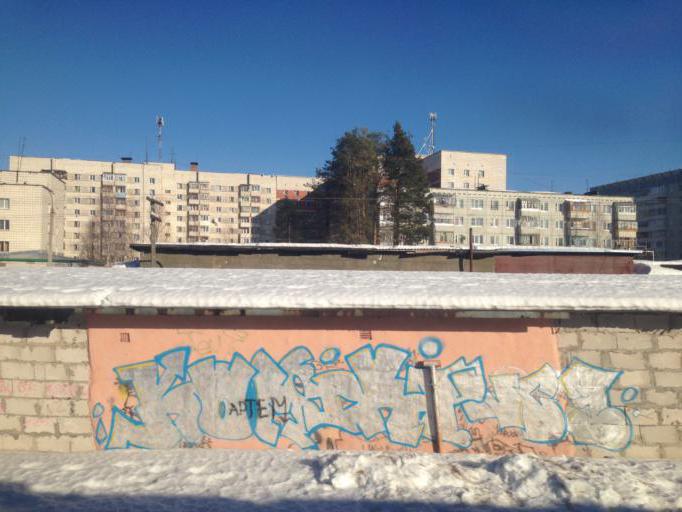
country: RU
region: Komi Republic
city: Ezhva
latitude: 61.7870
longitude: 50.7390
